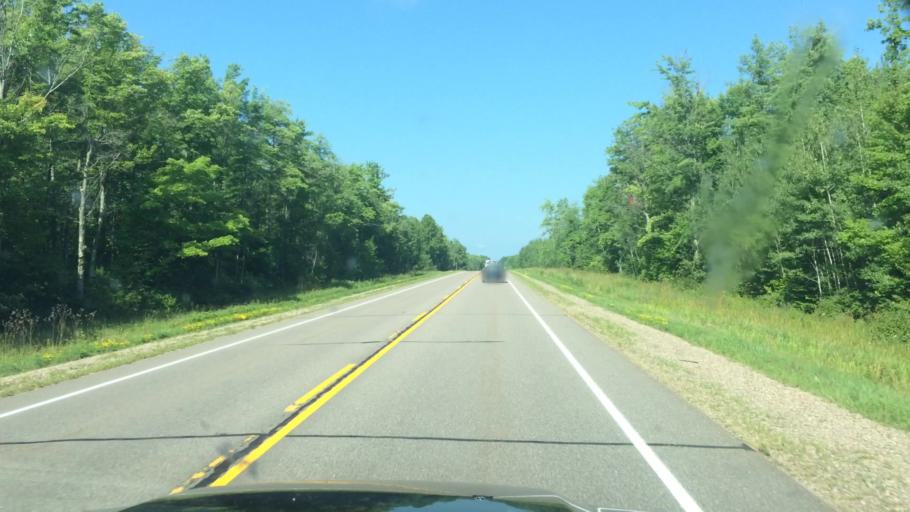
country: US
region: Wisconsin
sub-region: Langlade County
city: Antigo
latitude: 45.1469
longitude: -89.3618
